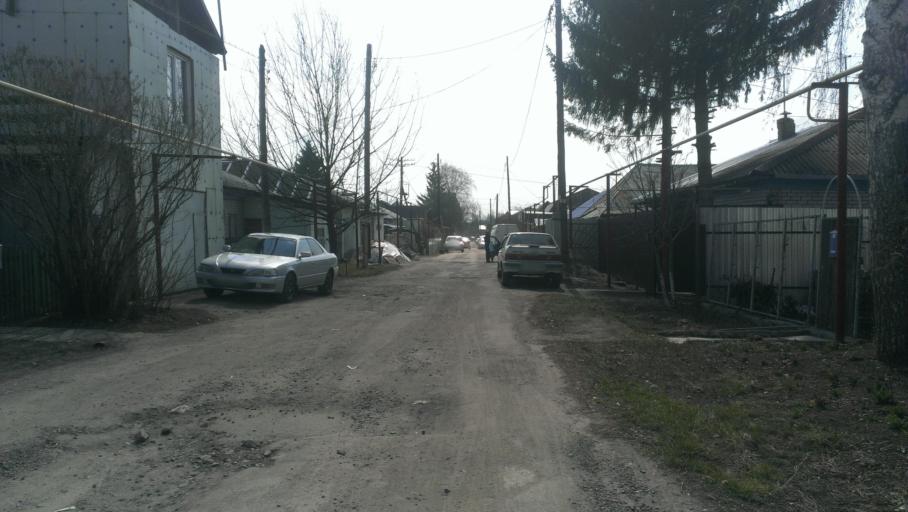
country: RU
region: Altai Krai
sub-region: Gorod Barnaulskiy
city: Barnaul
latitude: 53.3553
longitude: 83.6916
